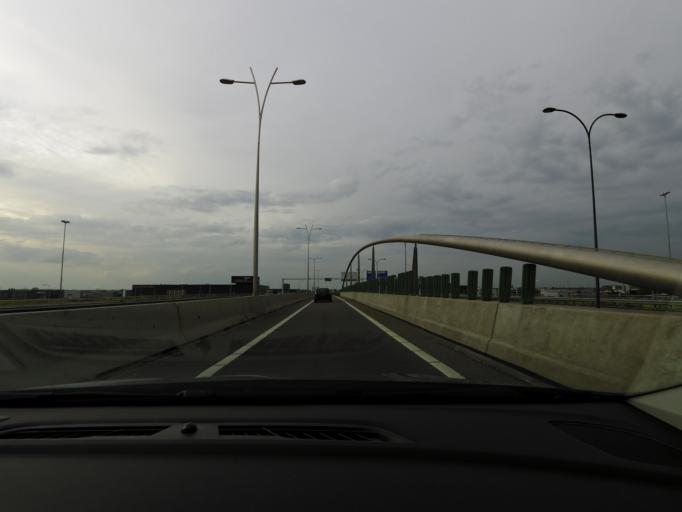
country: NL
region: North Brabant
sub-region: Gemeente Waalwijk
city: Waalwijk
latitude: 51.6908
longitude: 5.0406
